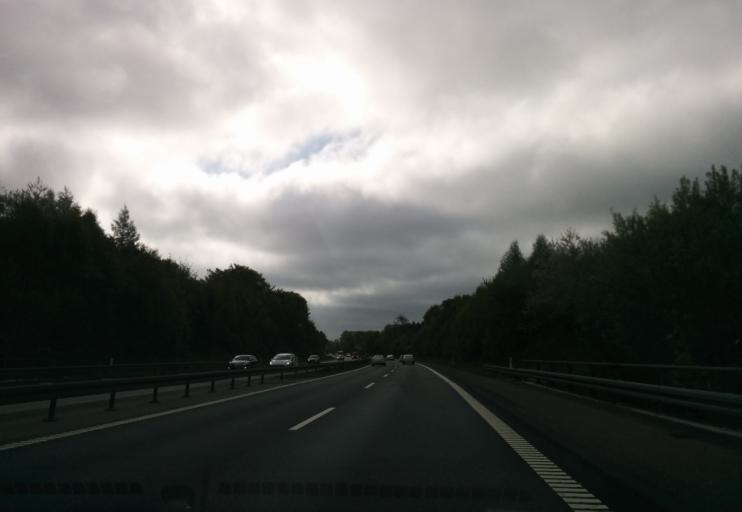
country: DK
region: South Denmark
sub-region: Fredericia Kommune
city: Taulov
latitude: 55.5631
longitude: 9.6203
